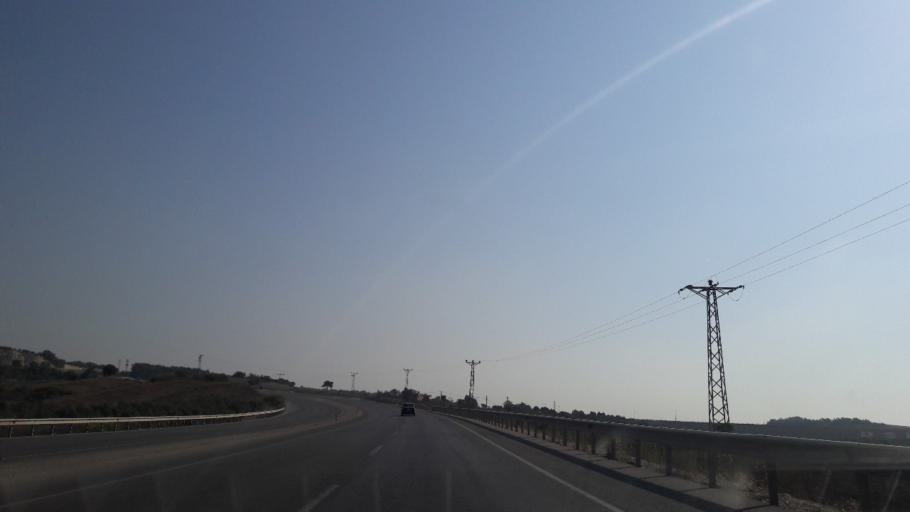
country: TR
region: Adana
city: Yuregir
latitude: 37.0741
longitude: 35.4655
